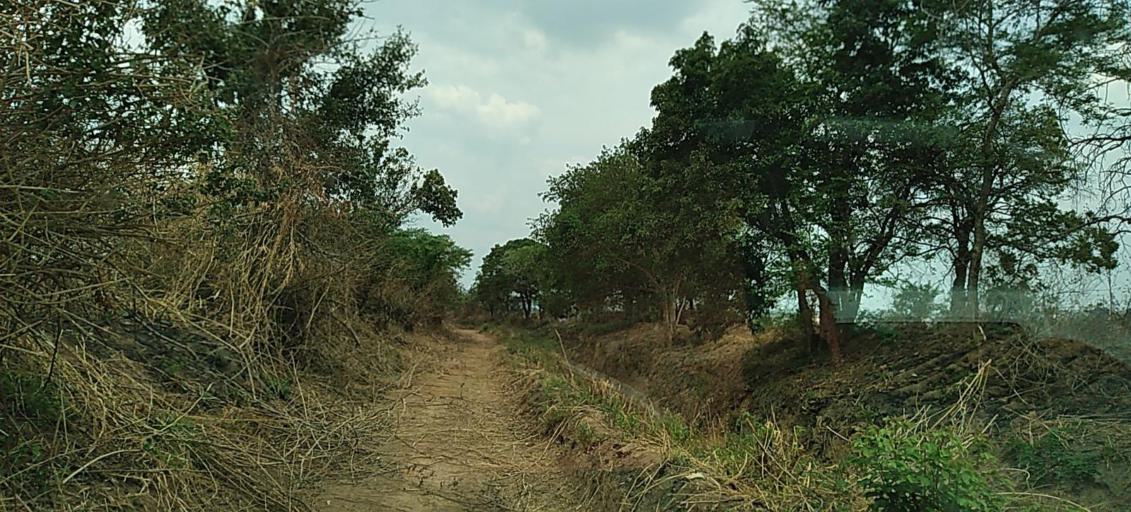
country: ZM
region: Copperbelt
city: Chililabombwe
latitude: -12.3603
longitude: 27.8017
